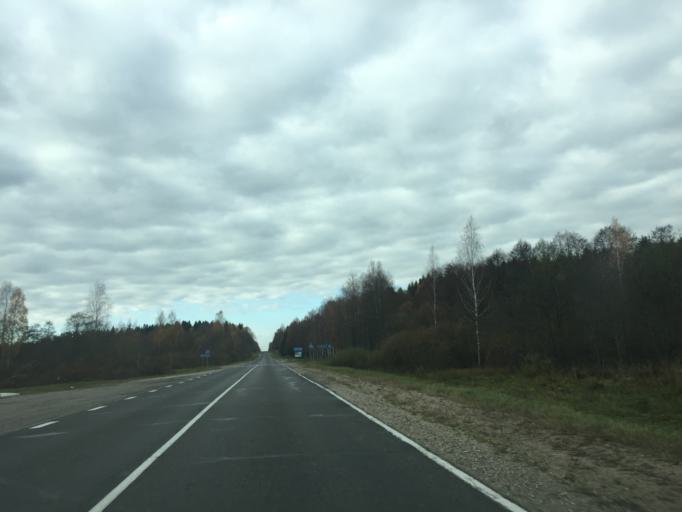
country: BY
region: Vitebsk
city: Mosar
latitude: 55.0675
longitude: 27.3443
